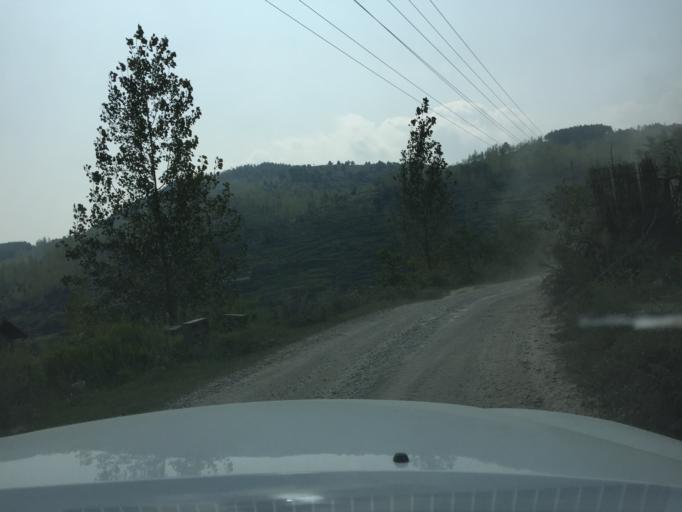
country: CN
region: Guizhou Sheng
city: Longquan
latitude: 28.2748
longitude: 108.0365
